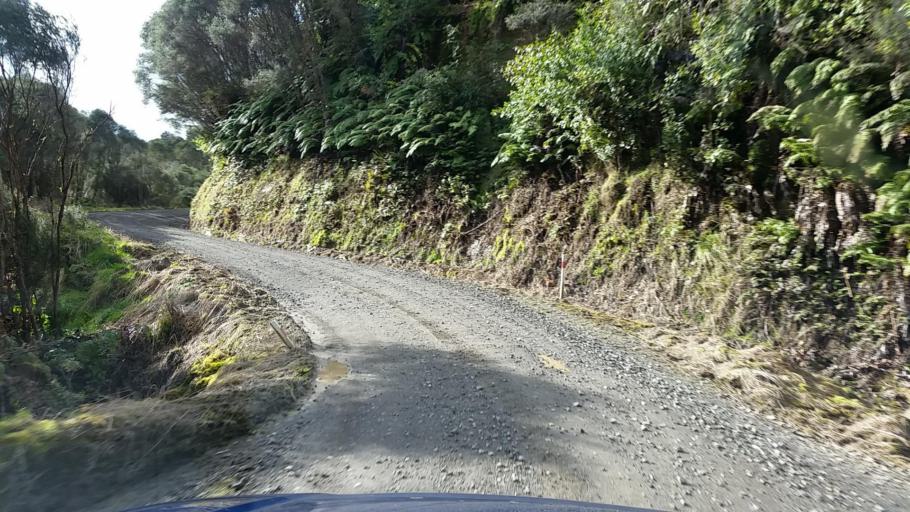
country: NZ
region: Taranaki
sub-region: South Taranaki District
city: Eltham
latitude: -39.2727
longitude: 174.7655
